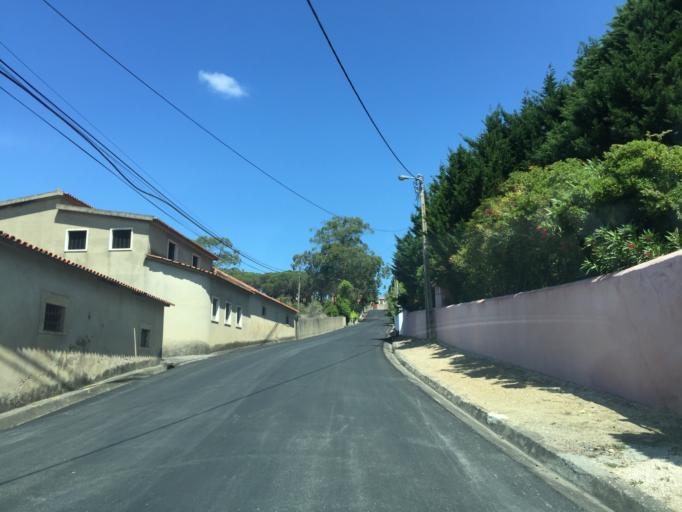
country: PT
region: Lisbon
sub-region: Sintra
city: Sintra
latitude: 38.8118
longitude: -9.4041
